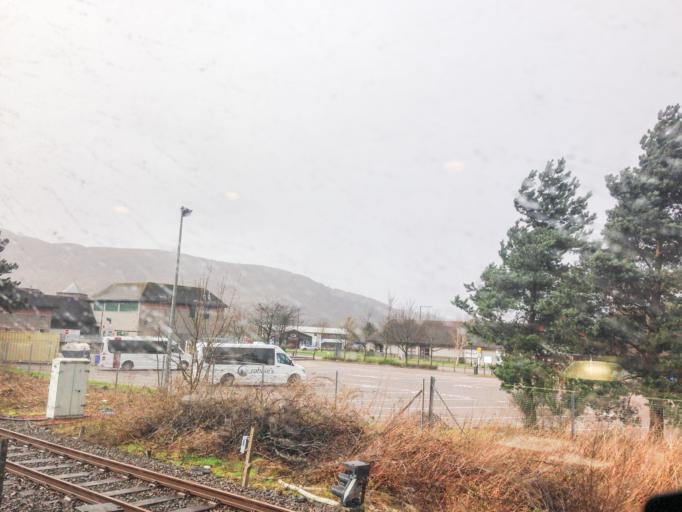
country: GB
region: Scotland
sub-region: Highland
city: Fort William
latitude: 56.8213
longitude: -5.1023
